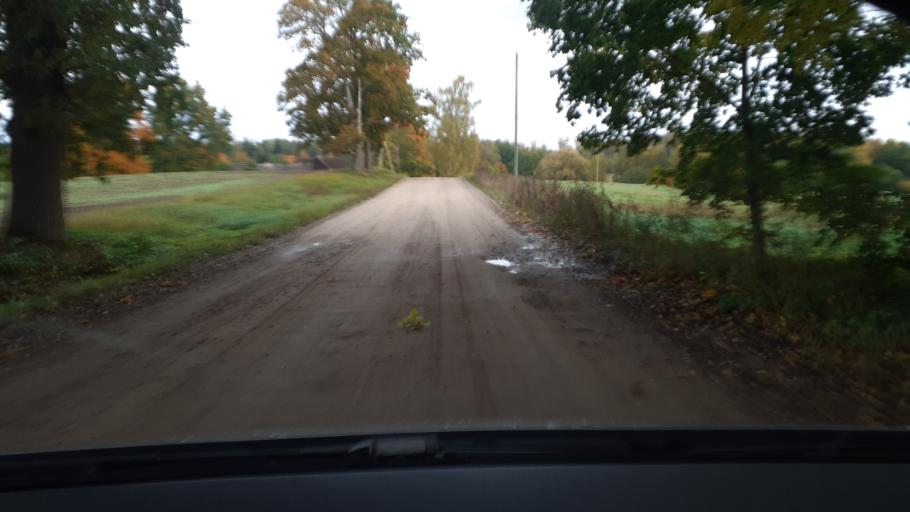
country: LV
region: Kuldigas Rajons
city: Kuldiga
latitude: 57.0251
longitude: 21.9143
